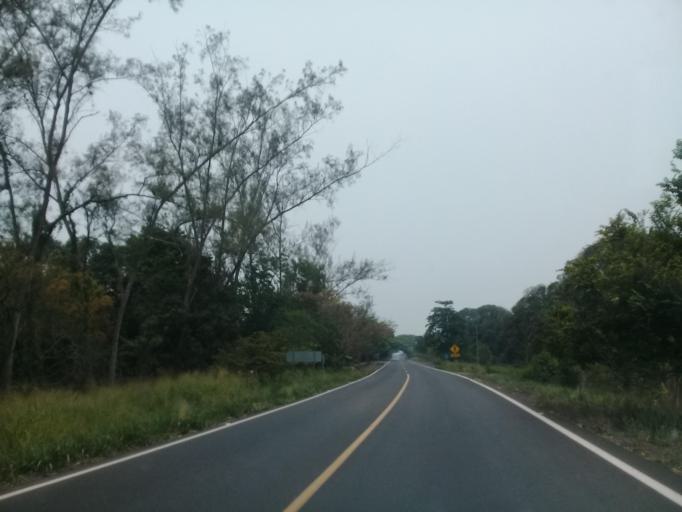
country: MX
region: Veracruz
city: Paso del Toro
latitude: 18.9732
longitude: -96.1791
